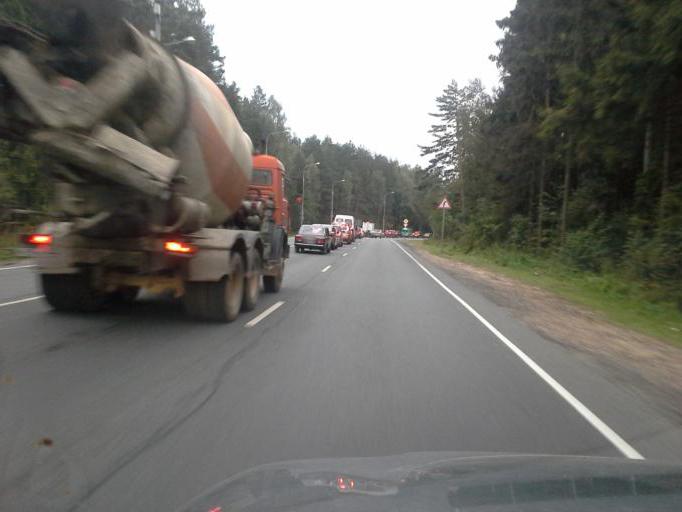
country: RU
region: Moskovskaya
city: Zhavoronki
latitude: 55.6585
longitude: 37.0965
